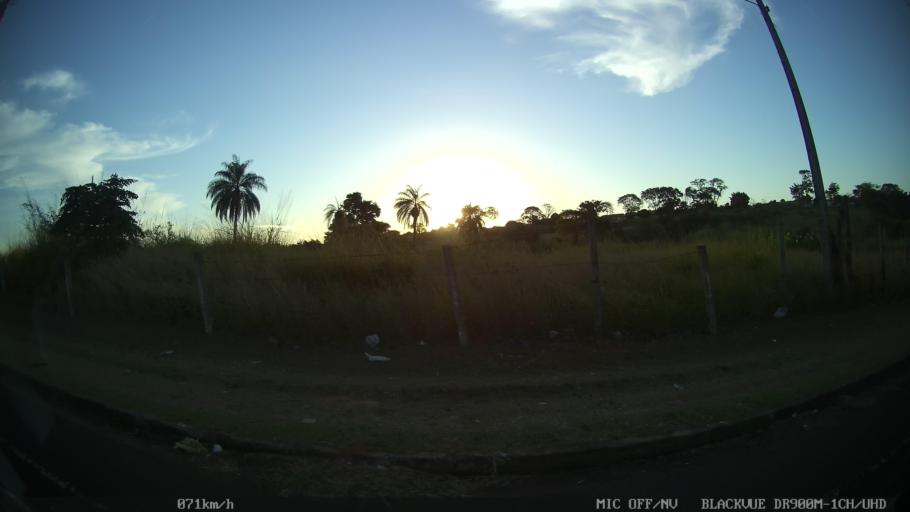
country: BR
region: Sao Paulo
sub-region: Franca
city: Franca
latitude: -20.5113
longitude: -47.4137
